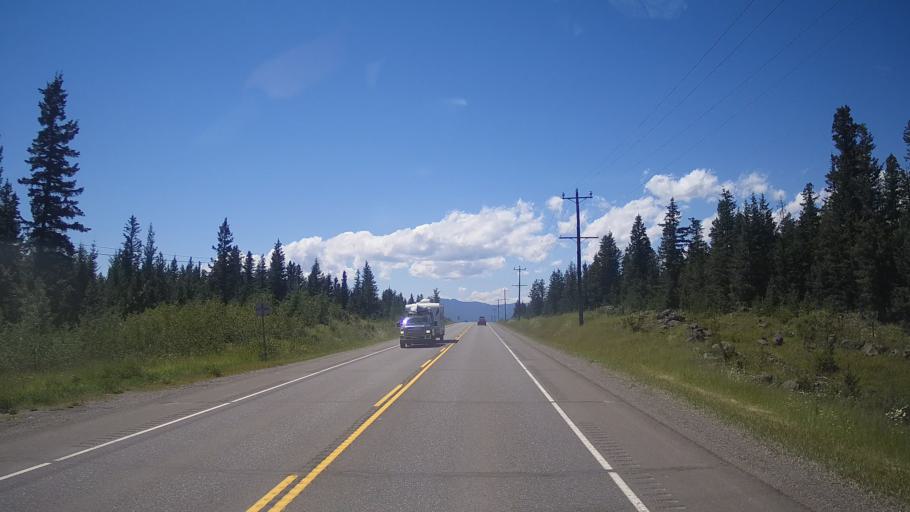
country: CA
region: British Columbia
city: Cache Creek
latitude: 51.2139
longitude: -121.5243
